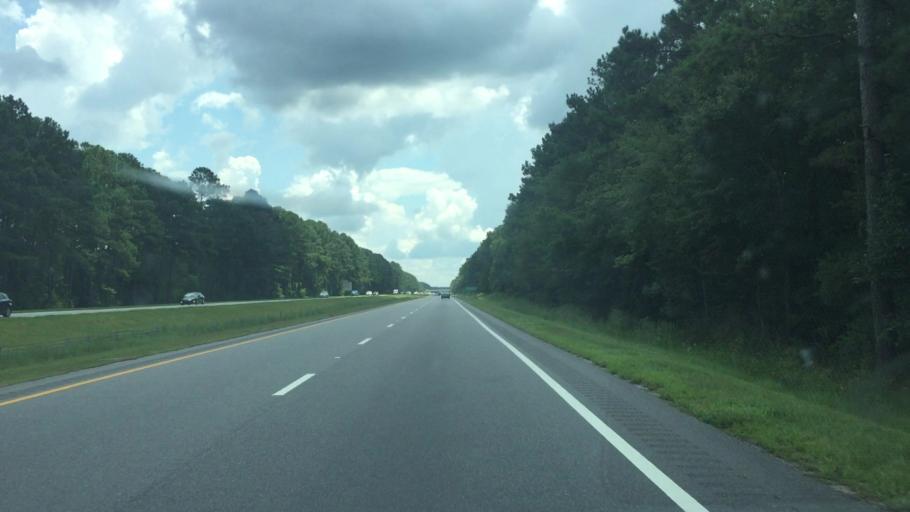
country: US
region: North Carolina
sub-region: Columbus County
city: Chadbourn
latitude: 34.3930
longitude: -78.8902
